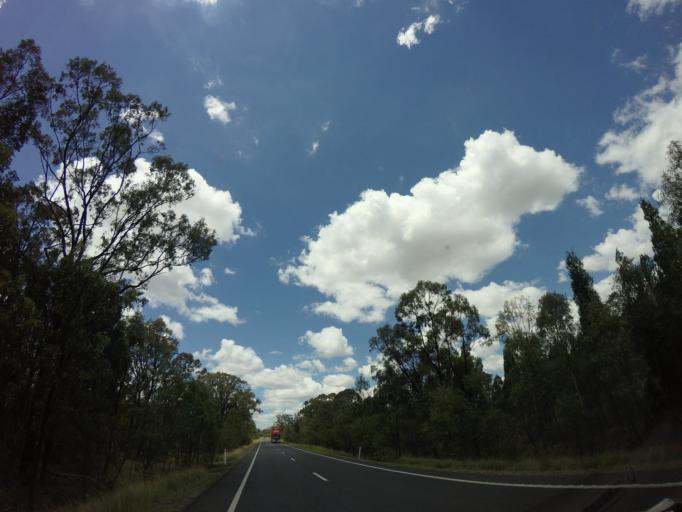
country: AU
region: Queensland
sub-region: Toowoomba
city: Oakey
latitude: -27.9125
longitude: 151.1838
